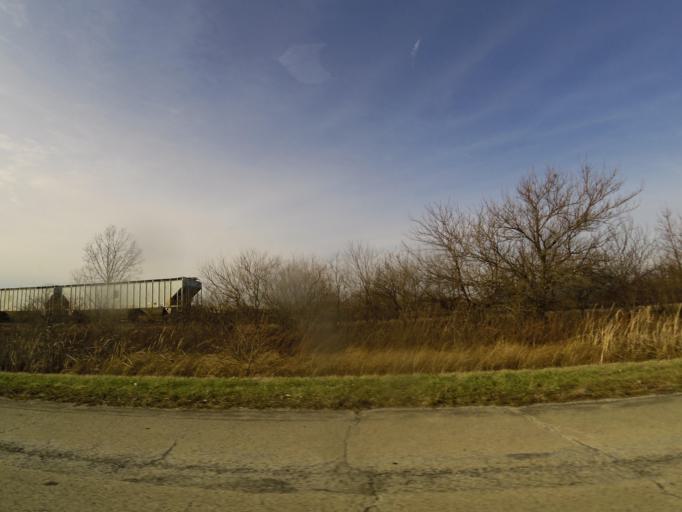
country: US
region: Illinois
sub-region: Macon County
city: Macon
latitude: 39.7674
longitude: -88.9829
